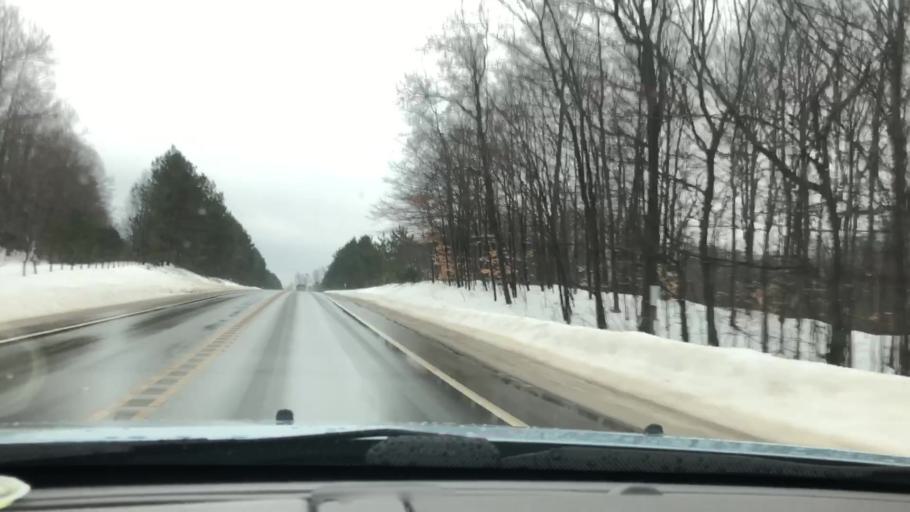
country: US
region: Michigan
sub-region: Charlevoix County
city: East Jordan
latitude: 45.1005
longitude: -85.0281
